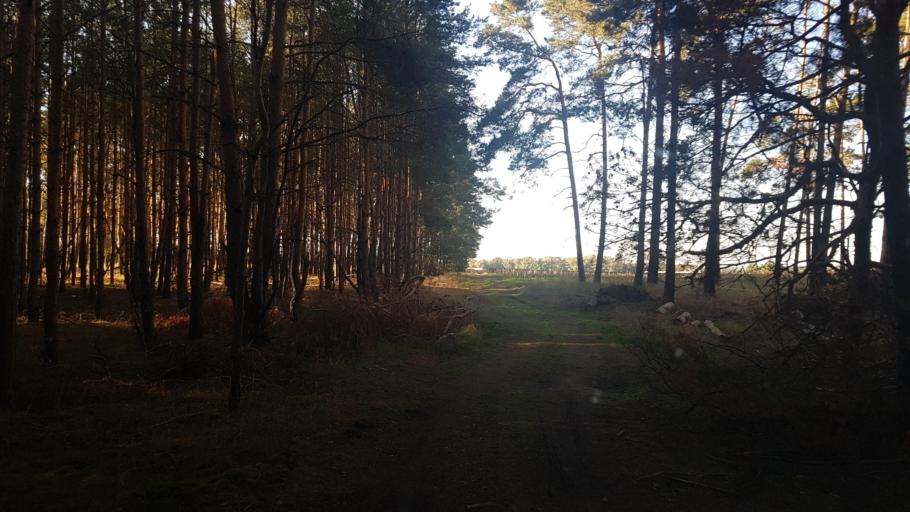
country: DE
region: Brandenburg
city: Herzberg
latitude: 51.6652
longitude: 13.3063
